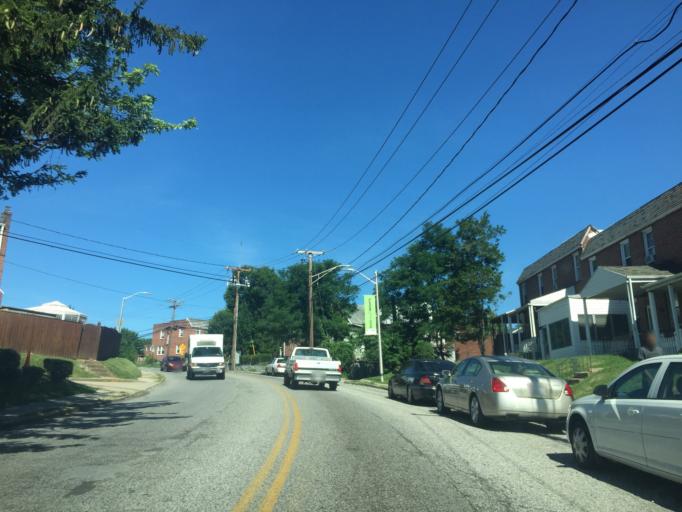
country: US
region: Maryland
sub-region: Baltimore County
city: Lochearn
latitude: 39.3409
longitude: -76.6630
